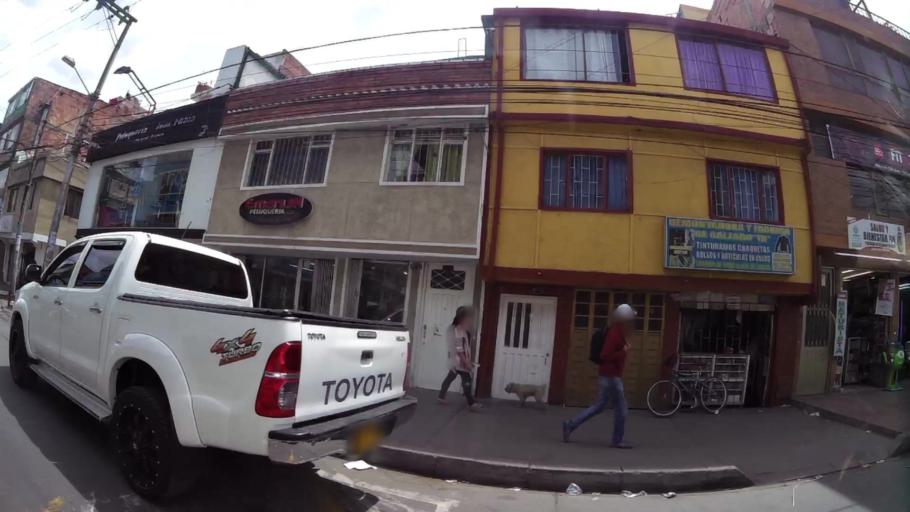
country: CO
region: Cundinamarca
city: Soacha
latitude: 4.6363
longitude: -74.1655
